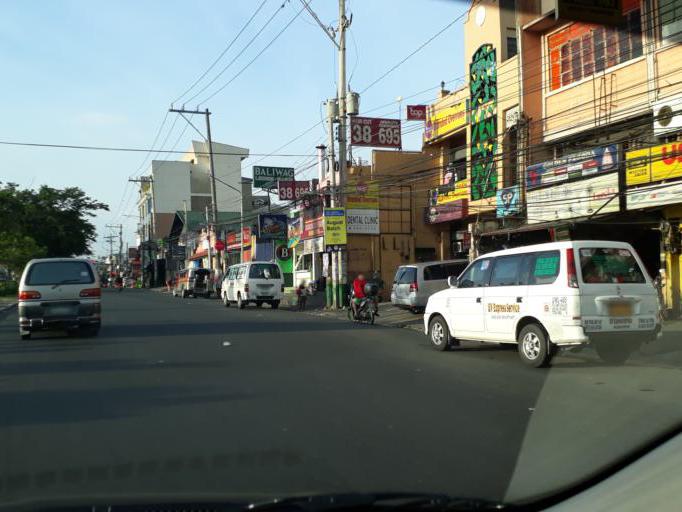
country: PH
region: Calabarzon
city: Bagong Pagasa
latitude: 14.6588
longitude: 121.0199
